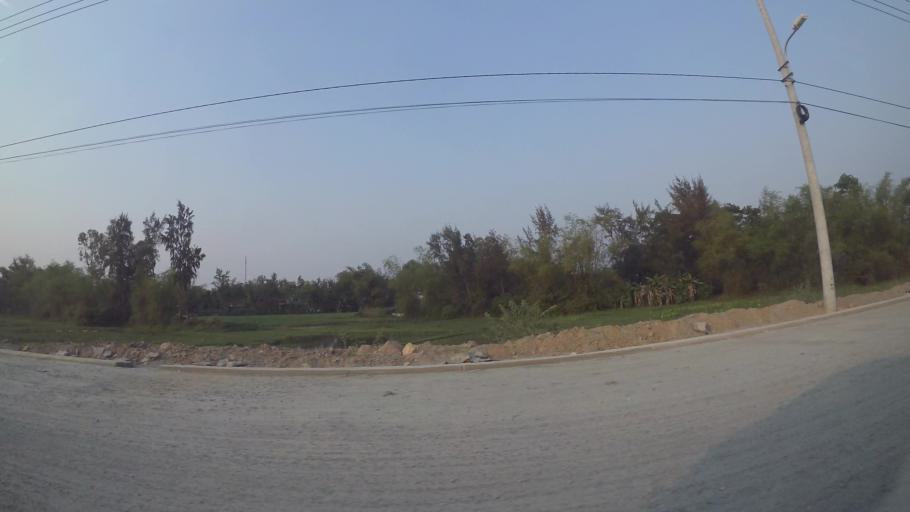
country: VN
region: Da Nang
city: Ngu Hanh Son
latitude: 15.9555
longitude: 108.2381
